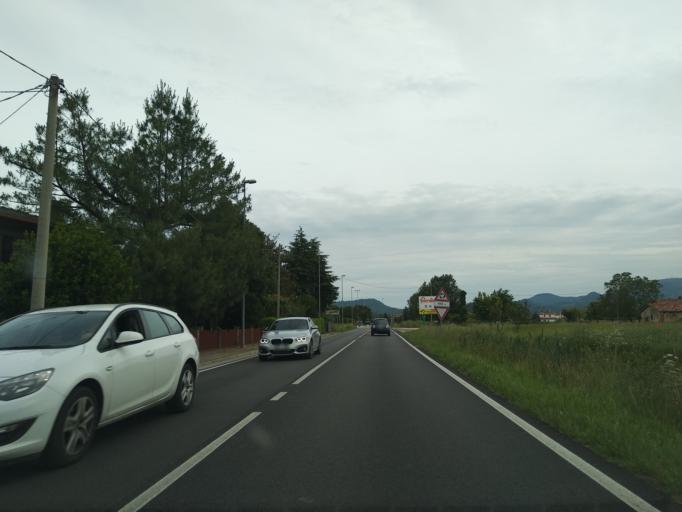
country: IT
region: Veneto
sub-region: Provincia di Padova
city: Montemerlo
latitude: 45.3985
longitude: 11.6961
